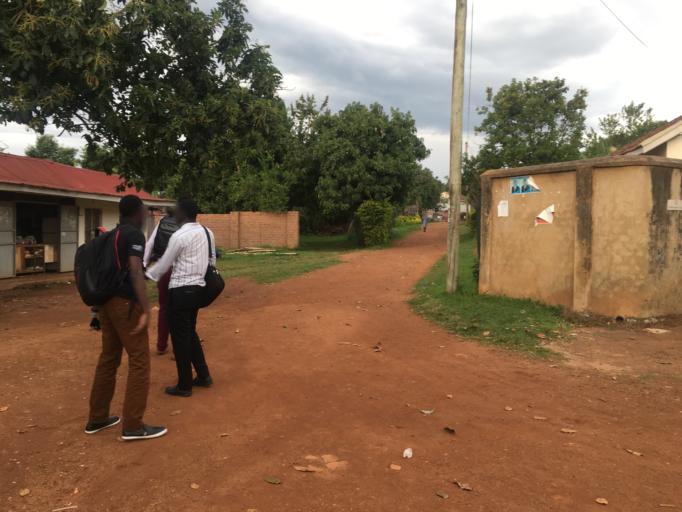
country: UG
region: Central Region
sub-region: Wakiso District
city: Entebbe
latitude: 0.0518
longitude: 32.4630
